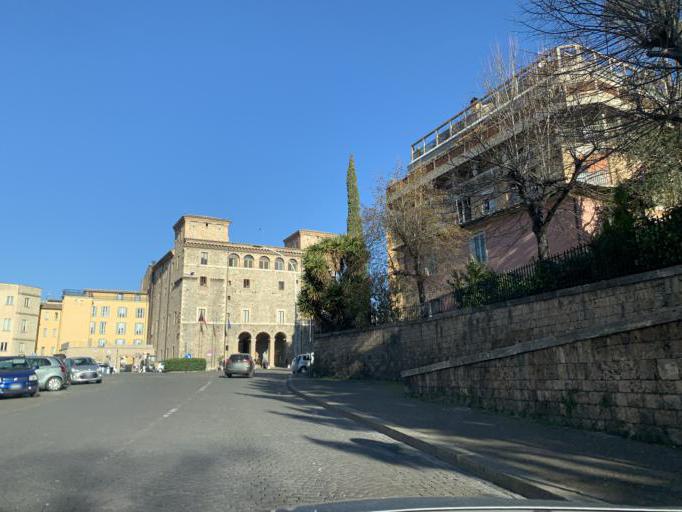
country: IT
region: Umbria
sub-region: Provincia di Terni
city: Terni
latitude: 42.5600
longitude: 12.6477
